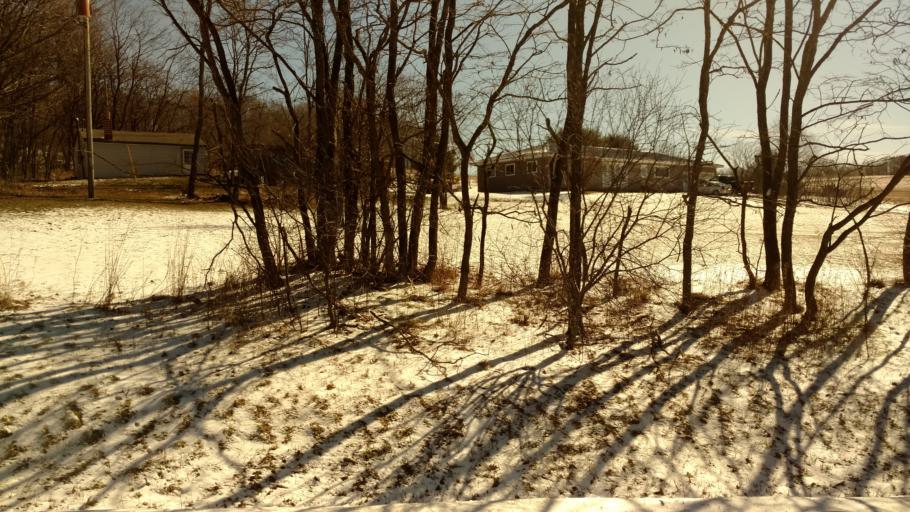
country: US
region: New York
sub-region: Allegany County
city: Wellsville
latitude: 42.0817
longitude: -78.0066
